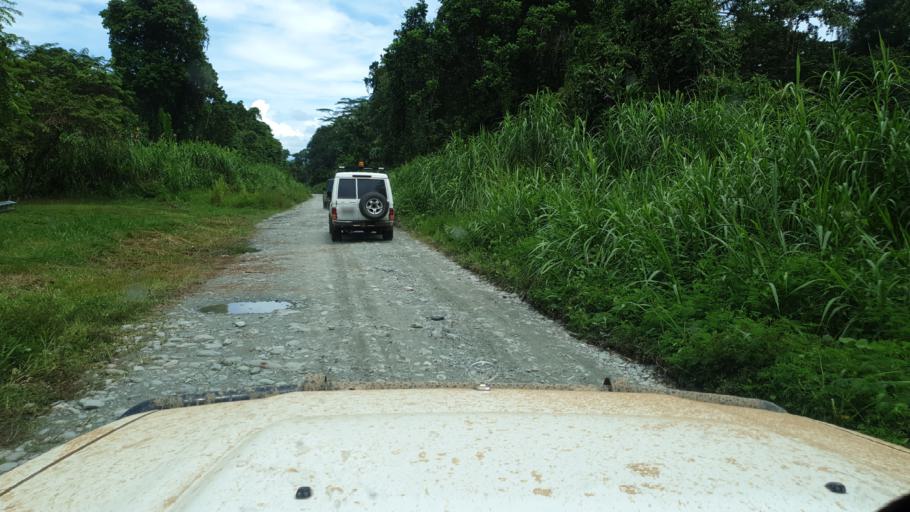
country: PG
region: Northern Province
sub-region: Sohe
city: Kokoda
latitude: -8.9163
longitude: 147.9151
